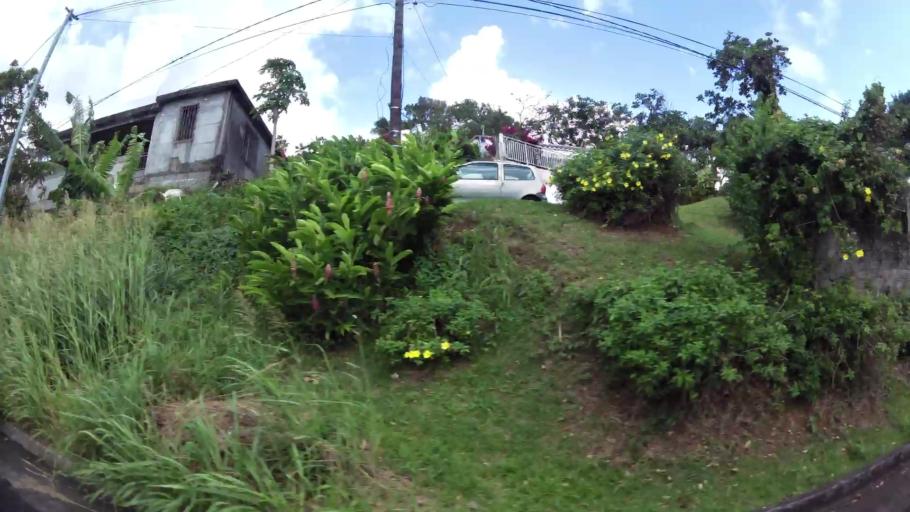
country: GP
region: Guadeloupe
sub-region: Guadeloupe
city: Trois-Rivieres
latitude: 15.9948
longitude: -61.6089
